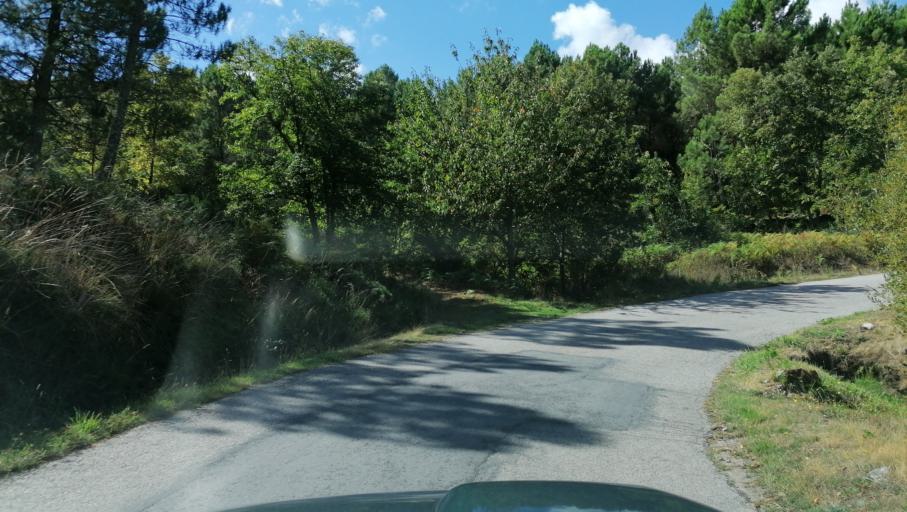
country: PT
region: Vila Real
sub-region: Vila Pouca de Aguiar
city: Vila Pouca de Aguiar
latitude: 41.5564
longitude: -7.6489
